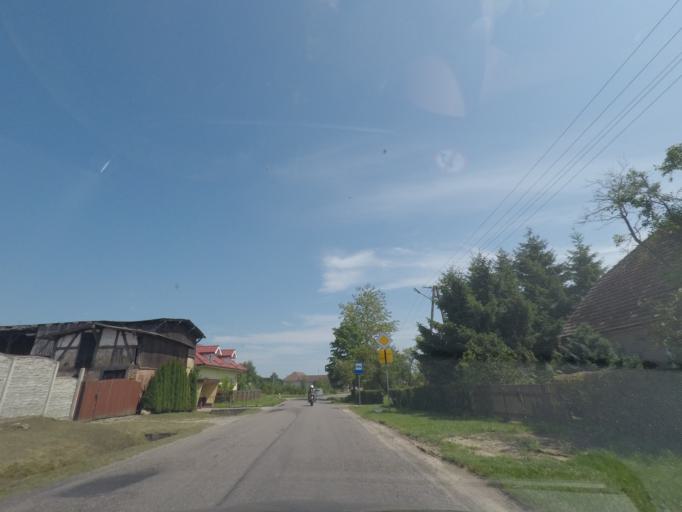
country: PL
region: West Pomeranian Voivodeship
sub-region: Powiat slawienski
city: Darlowo
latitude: 54.4621
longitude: 16.5239
